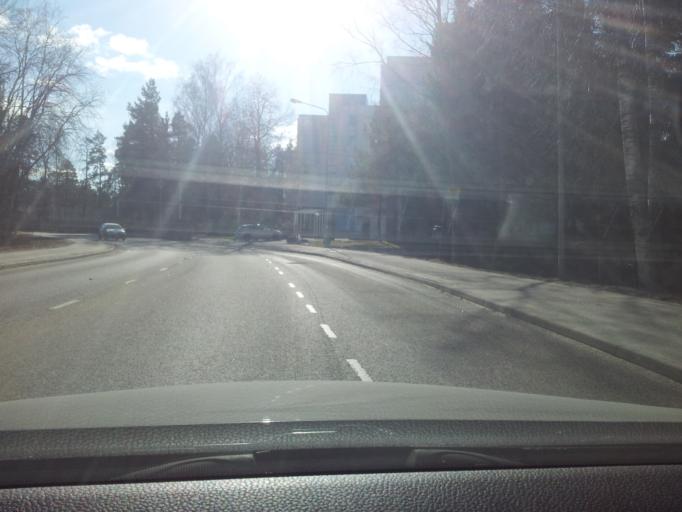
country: FI
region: Uusimaa
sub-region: Helsinki
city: Koukkuniemi
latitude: 60.1607
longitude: 24.7900
